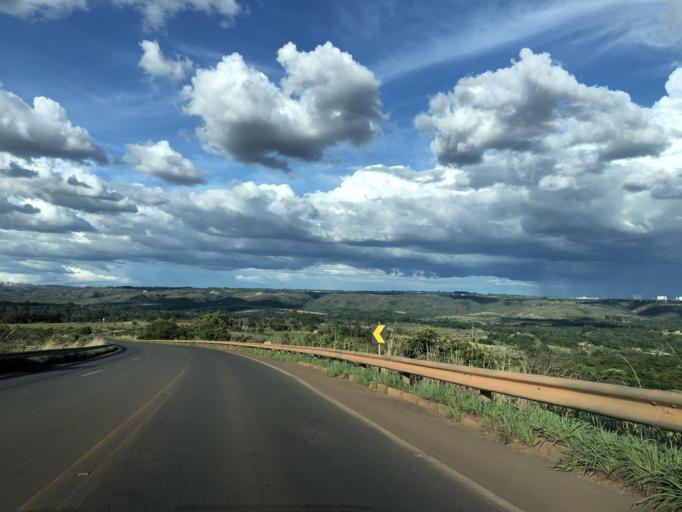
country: BR
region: Goias
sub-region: Luziania
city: Luziania
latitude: -16.0138
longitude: -48.1368
